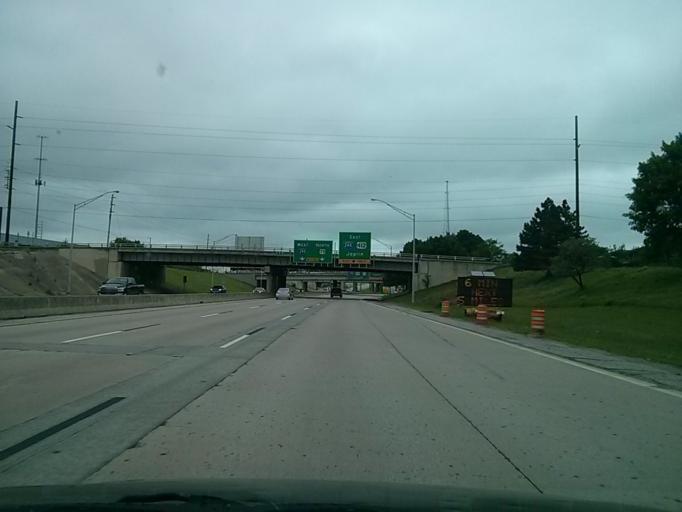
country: US
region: Oklahoma
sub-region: Tulsa County
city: Tulsa
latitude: 36.1546
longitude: -95.9802
